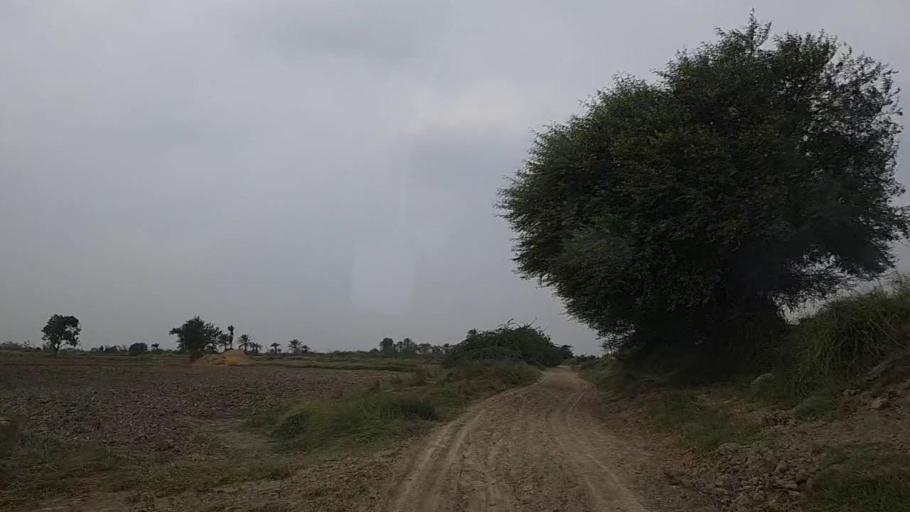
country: PK
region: Sindh
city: Mirpur Sakro
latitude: 24.5939
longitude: 67.6986
